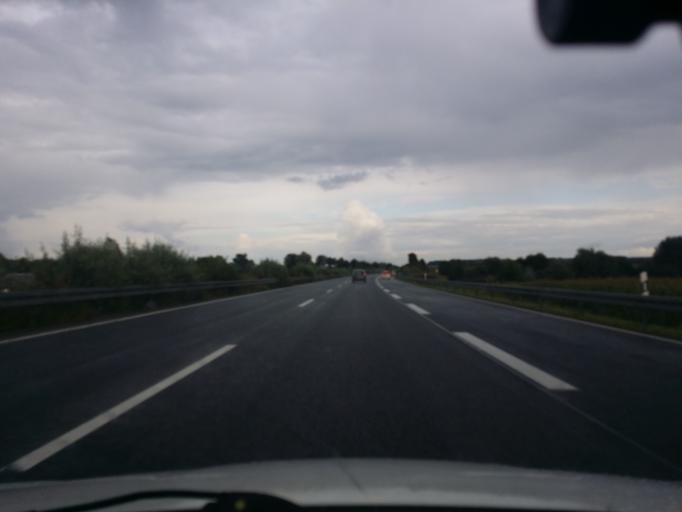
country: DE
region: Thuringia
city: Breitenworbis
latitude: 51.4033
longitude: 10.4091
